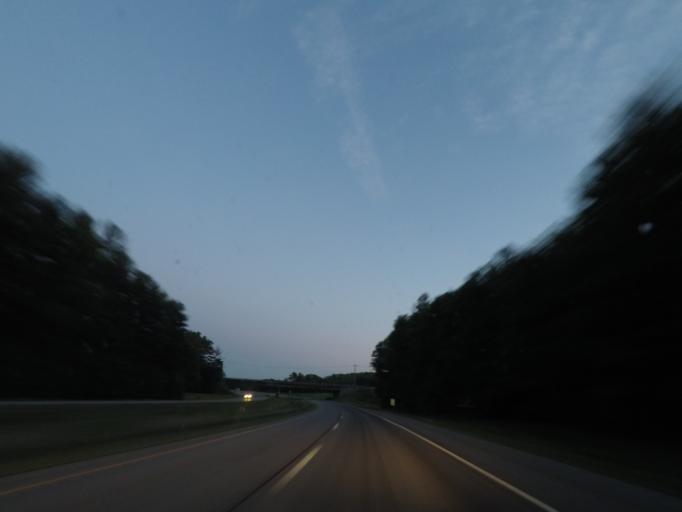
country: US
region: Connecticut
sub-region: Windham County
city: Putnam
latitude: 41.9014
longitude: -71.8989
